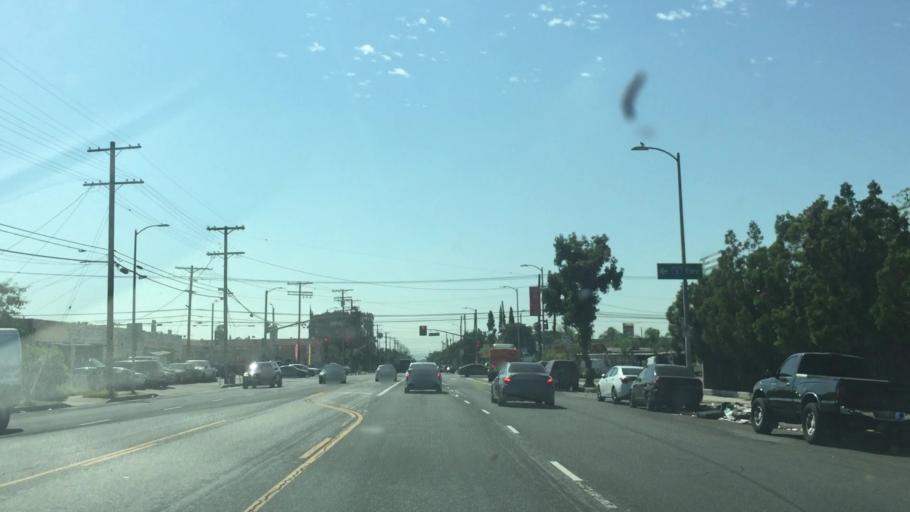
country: US
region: California
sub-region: Los Angeles County
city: San Fernando
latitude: 34.2547
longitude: -118.4395
